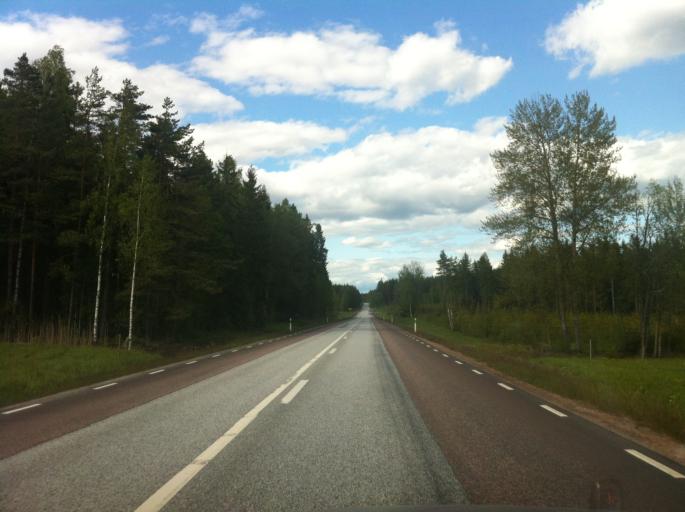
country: SE
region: Vaermland
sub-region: Storfors Kommun
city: Storfors
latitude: 59.5051
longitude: 14.2607
